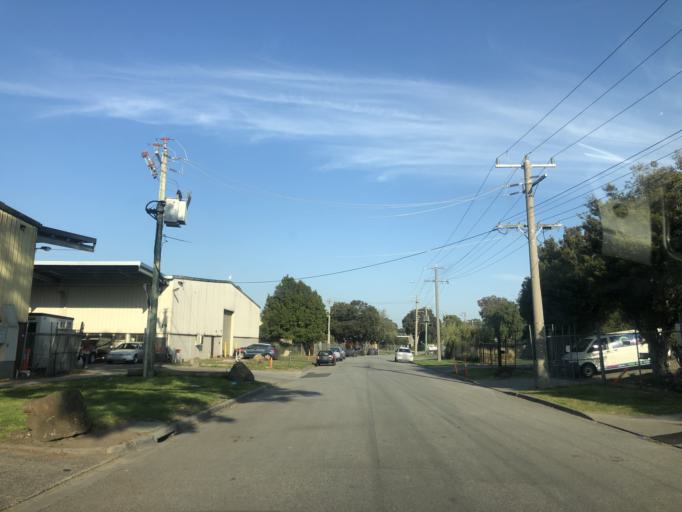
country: AU
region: Victoria
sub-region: Casey
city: Doveton
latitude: -38.0053
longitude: 145.2310
